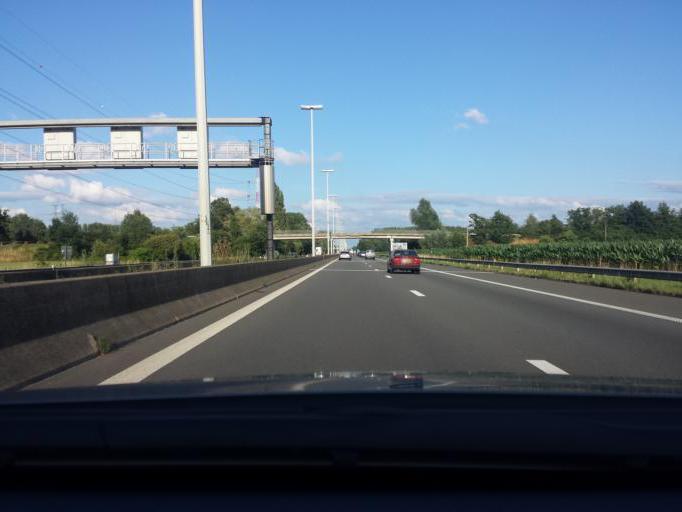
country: BE
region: Flanders
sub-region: Provincie Antwerpen
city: Ranst
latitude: 51.1958
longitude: 4.6143
